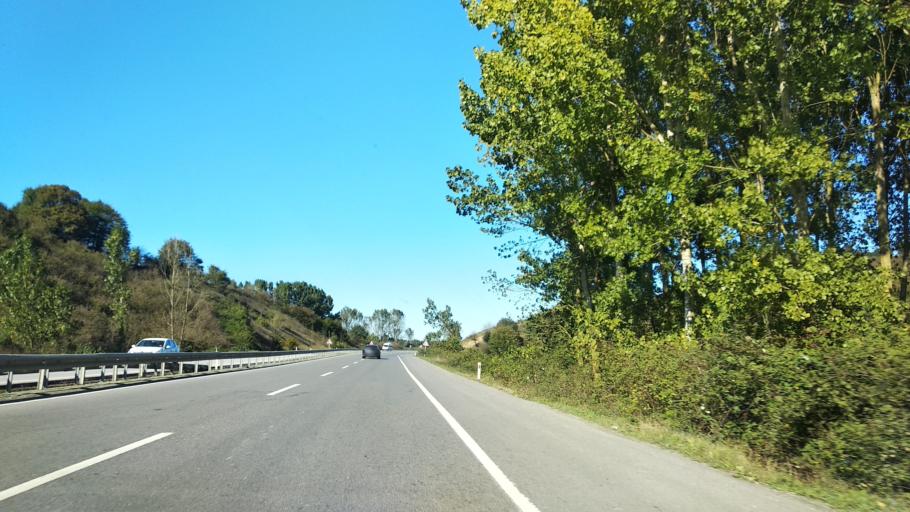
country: TR
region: Sakarya
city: Karasu
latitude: 41.0588
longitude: 30.6368
